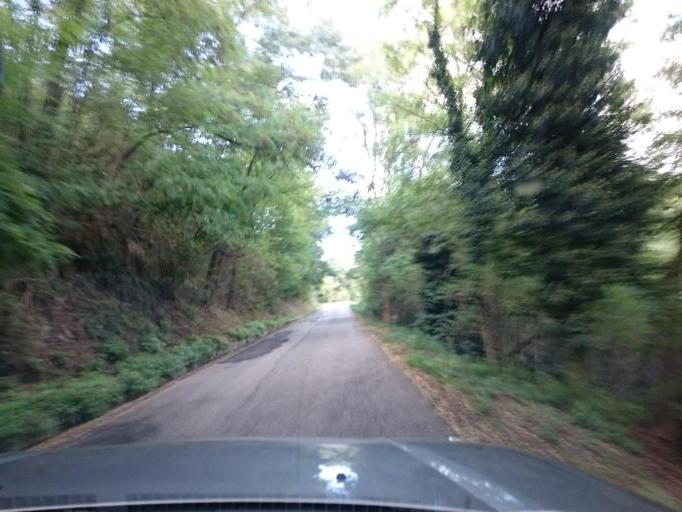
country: IT
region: Veneto
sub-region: Provincia di Padova
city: Galzignano
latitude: 45.3155
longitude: 11.7011
